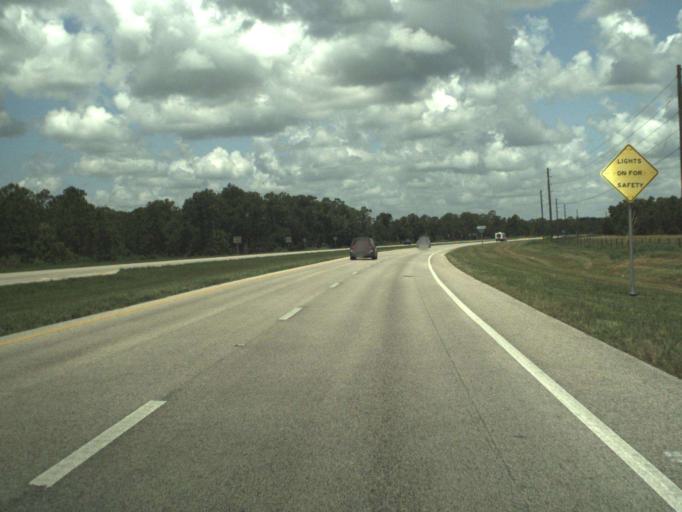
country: US
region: Florida
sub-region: Indian River County
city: Fellsmere
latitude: 27.6819
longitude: -80.8687
